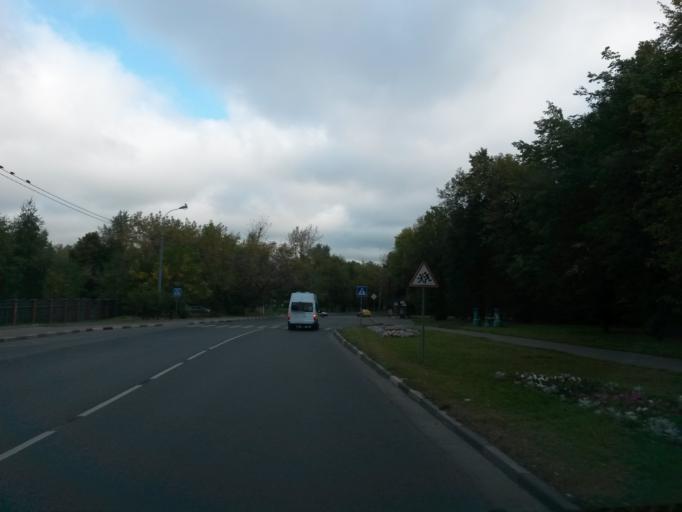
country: RU
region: Moscow
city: Kapotnya
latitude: 55.6387
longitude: 37.7933
